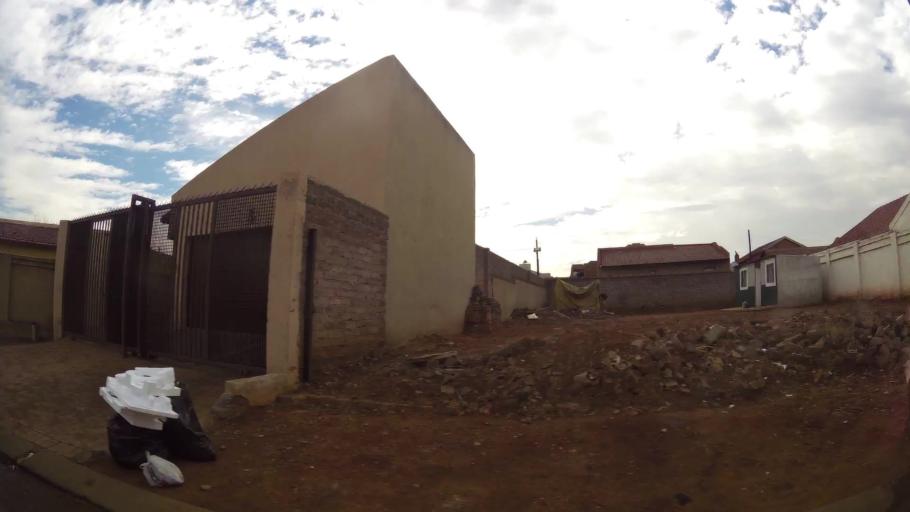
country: ZA
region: Gauteng
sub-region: Ekurhuleni Metropolitan Municipality
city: Germiston
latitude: -26.3200
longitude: 28.1786
